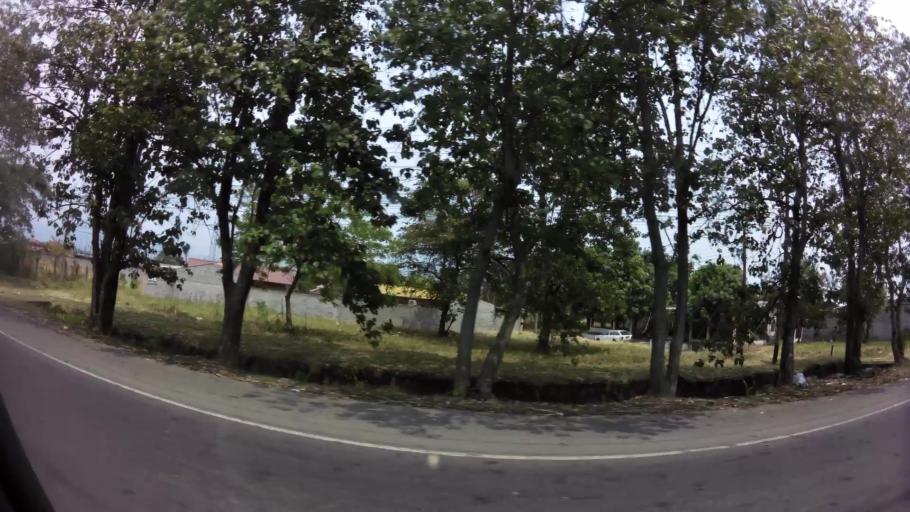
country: HN
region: Cortes
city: Villanueva
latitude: 15.3342
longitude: -87.9909
